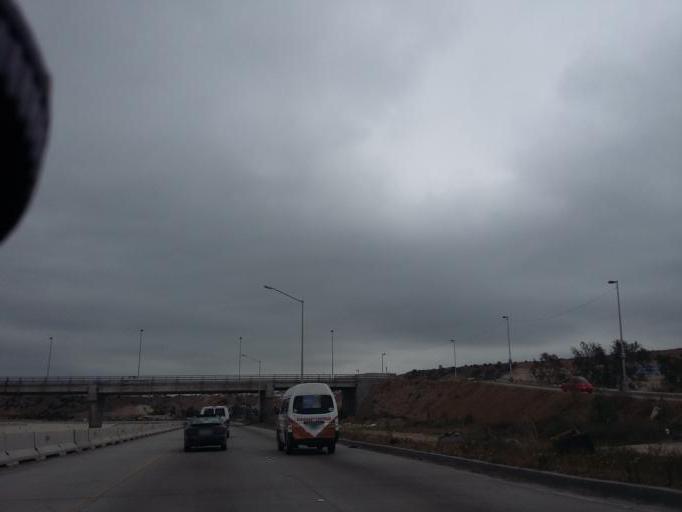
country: MX
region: Baja California
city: Tijuana
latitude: 32.5108
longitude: -116.9467
